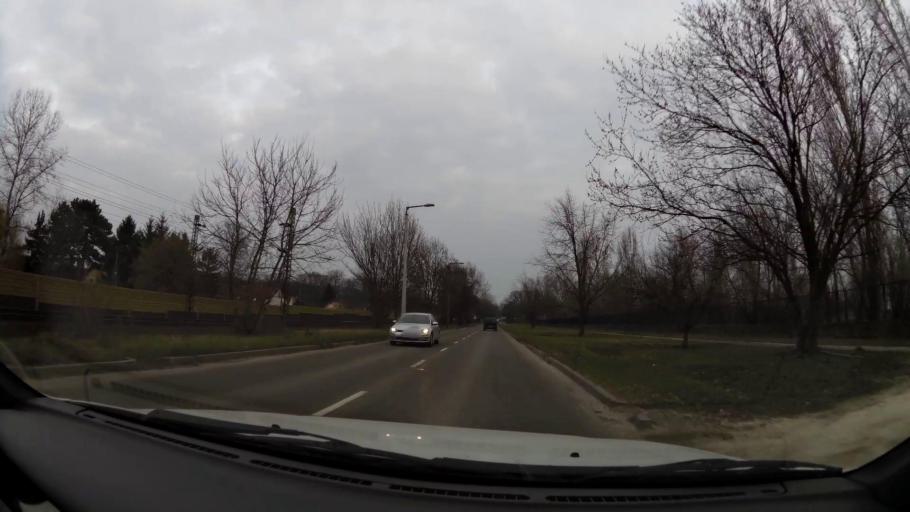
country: HU
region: Budapest
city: Budapest X. keruelet
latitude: 47.4813
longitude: 19.2061
